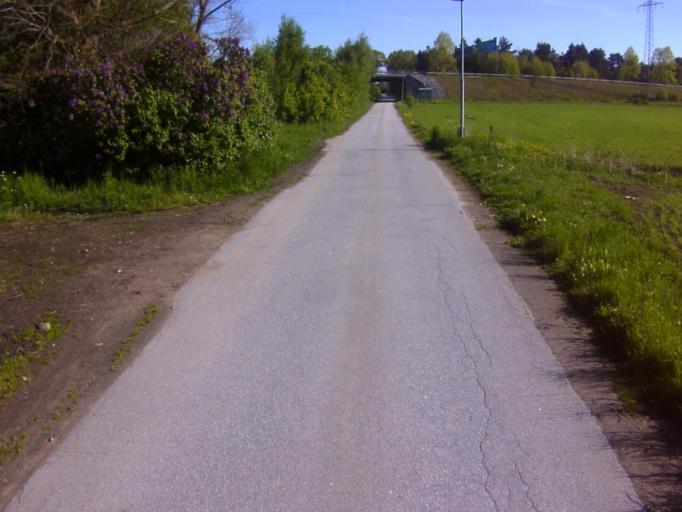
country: SE
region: Blekinge
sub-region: Solvesborgs Kommun
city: Soelvesborg
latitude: 56.0641
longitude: 14.6088
